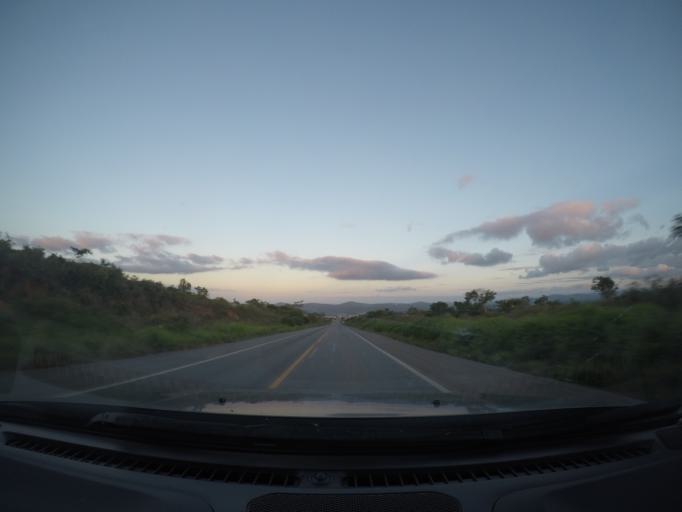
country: BR
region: Bahia
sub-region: Seabra
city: Seabra
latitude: -12.4337
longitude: -41.8188
